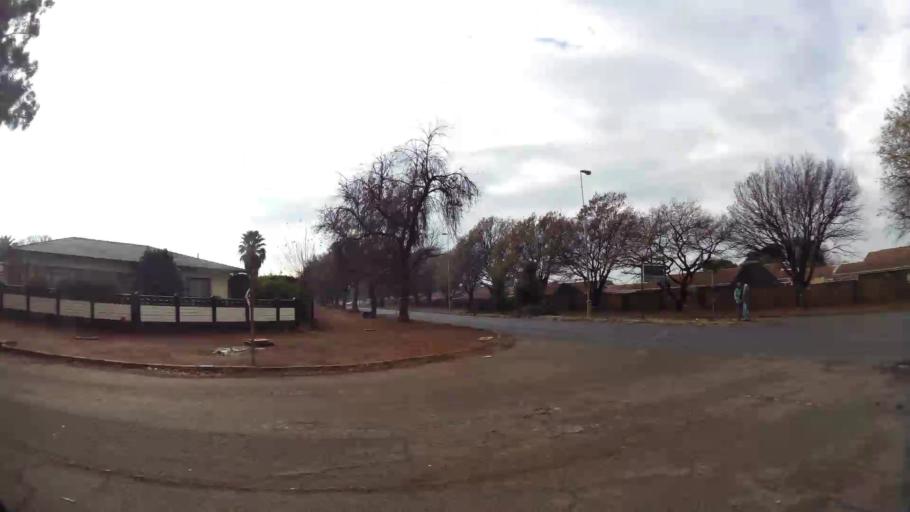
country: ZA
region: Gauteng
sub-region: Sedibeng District Municipality
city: Vanderbijlpark
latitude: -26.7040
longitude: 27.8282
